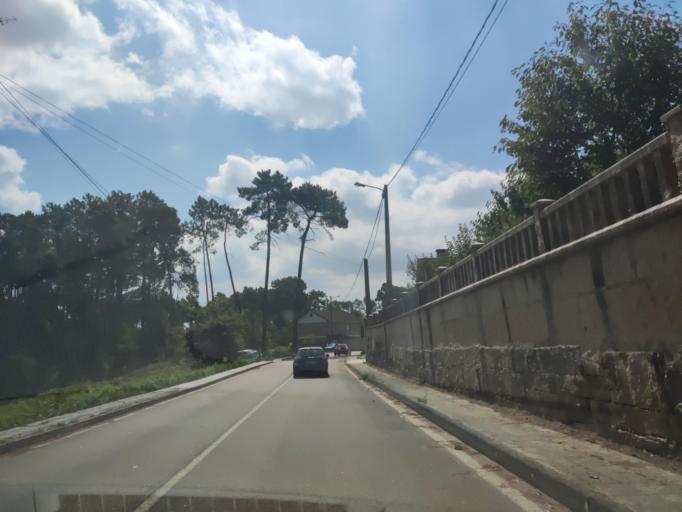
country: ES
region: Galicia
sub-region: Provincia de Pontevedra
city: Porrino
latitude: 42.1482
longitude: -8.6487
